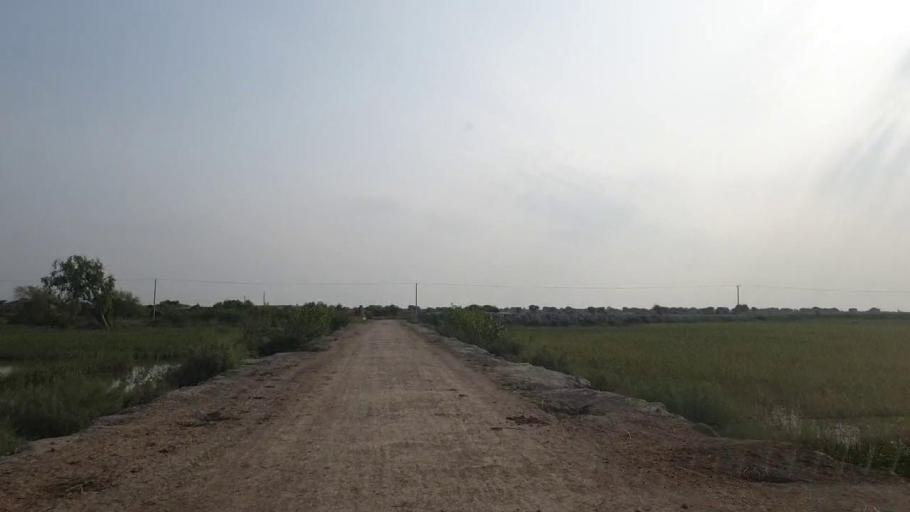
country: PK
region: Sindh
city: Kadhan
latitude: 24.4593
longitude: 68.8129
